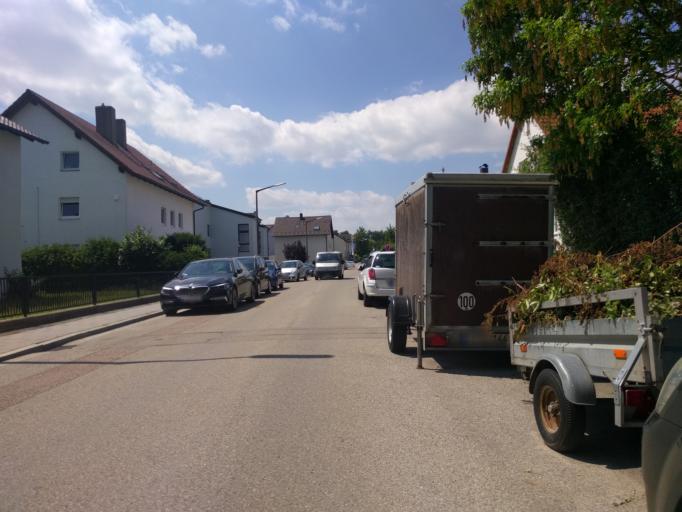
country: DE
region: Bavaria
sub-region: Upper Palatinate
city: Pentling
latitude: 48.9920
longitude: 12.0879
